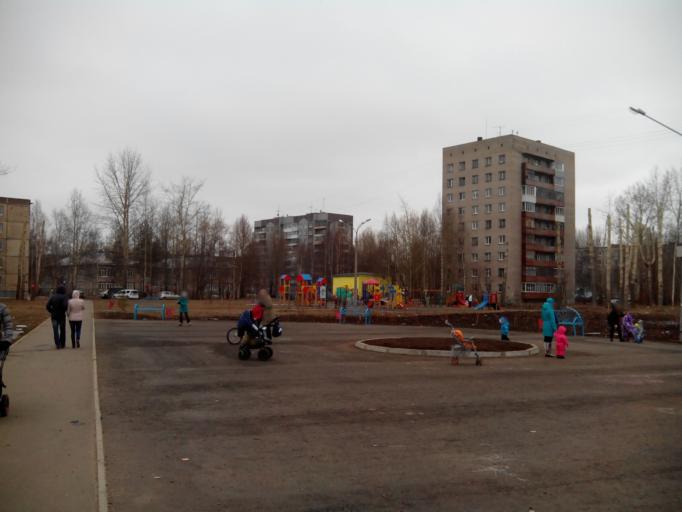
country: RU
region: Arkhangelskaya
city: Katunino
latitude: 64.5034
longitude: 40.6774
